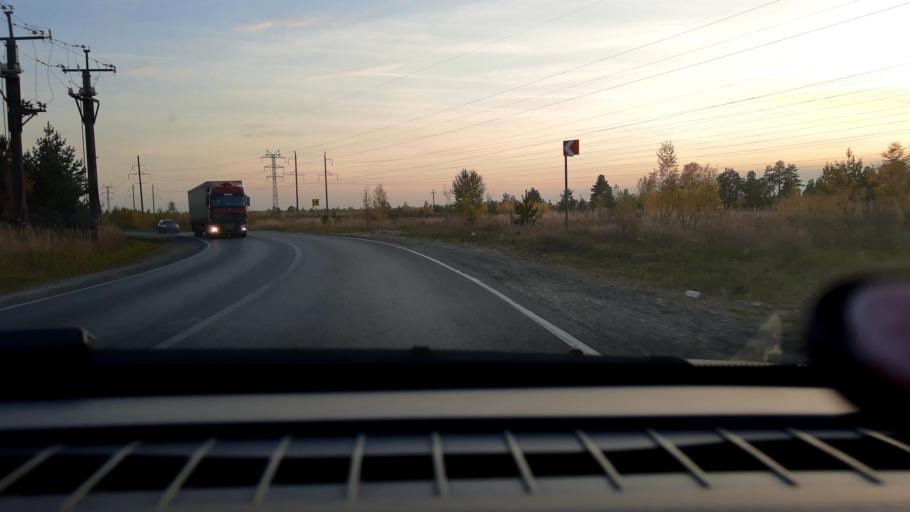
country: RU
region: Nizjnij Novgorod
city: Babino
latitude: 56.3270
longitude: 43.5595
